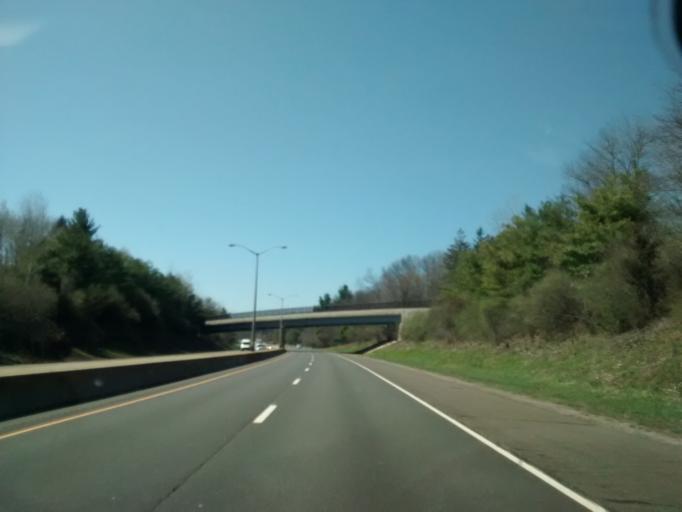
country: US
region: Connecticut
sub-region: Hartford County
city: East Hartford
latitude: 41.8000
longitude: -72.5812
